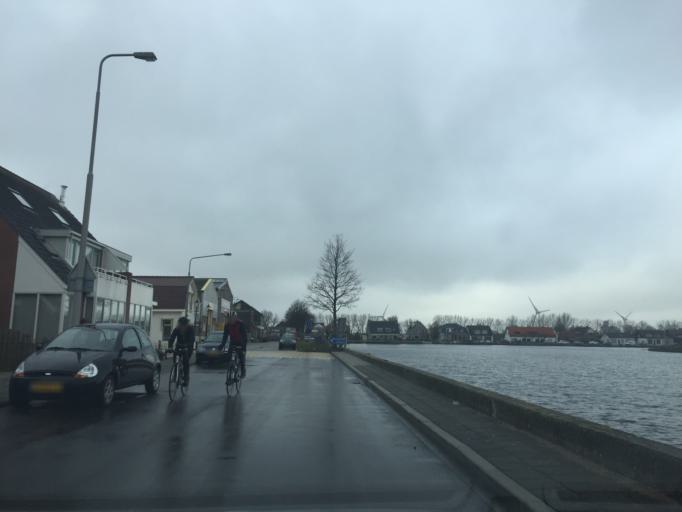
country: NL
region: South Holland
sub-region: Gemeente Kaag en Braassem
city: Oude Wetering
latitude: 52.2187
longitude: 4.6444
